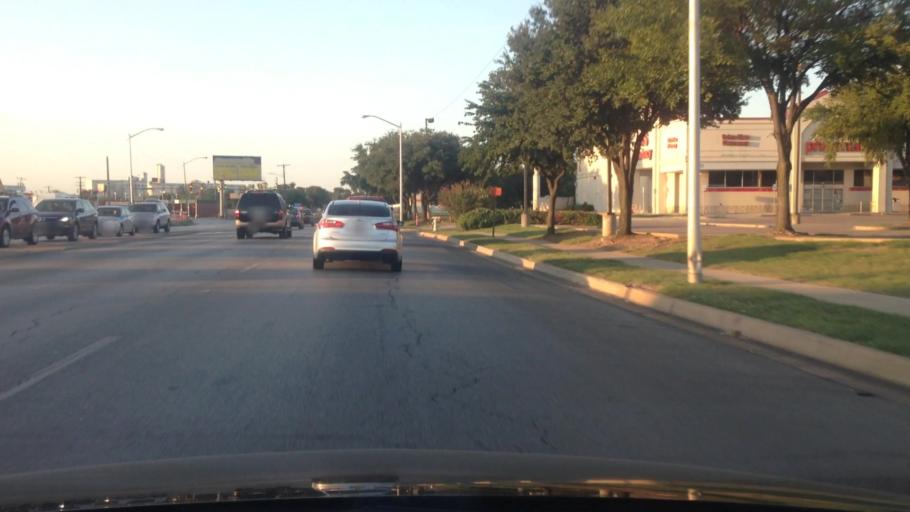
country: US
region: Texas
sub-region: Tarrant County
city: Haltom City
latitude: 32.7803
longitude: -97.2908
